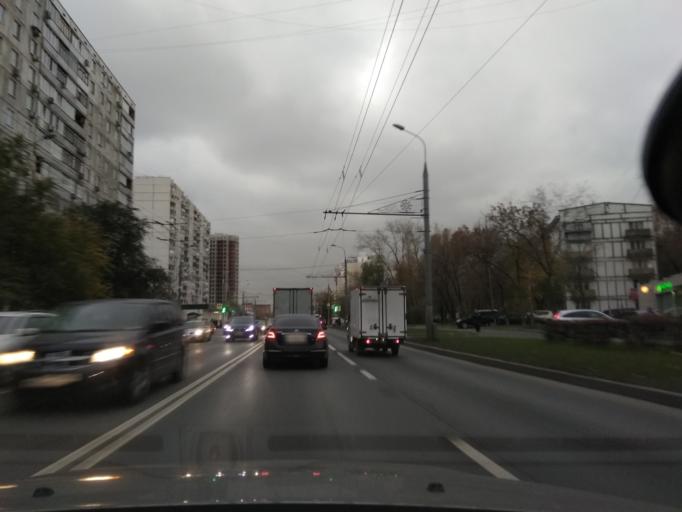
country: RU
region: Moscow
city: Novovladykino
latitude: 55.8264
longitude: 37.5823
